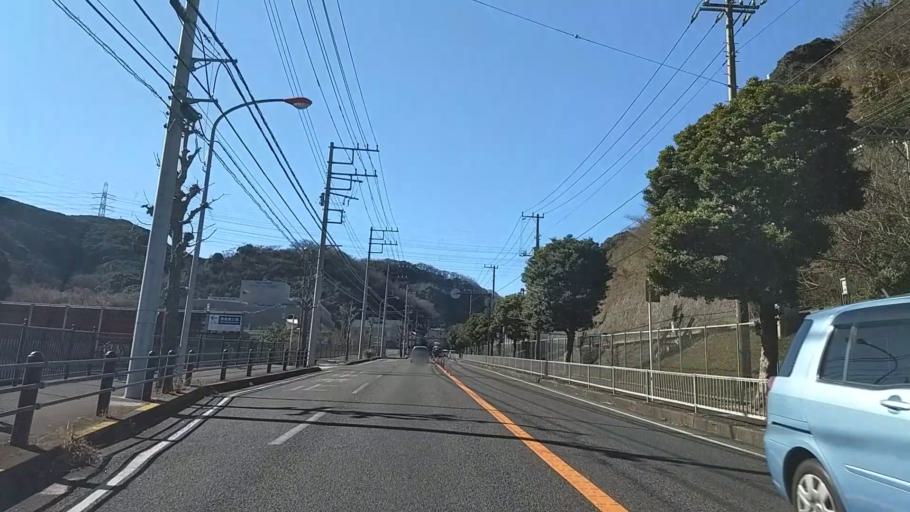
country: JP
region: Kanagawa
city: Yokosuka
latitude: 35.2248
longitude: 139.6990
